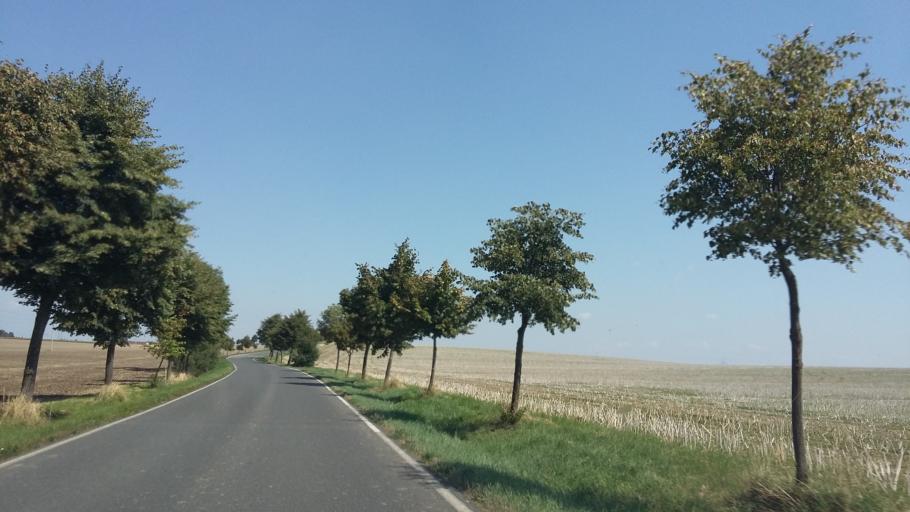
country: CZ
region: Central Bohemia
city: Zelenec
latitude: 50.1343
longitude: 14.6721
